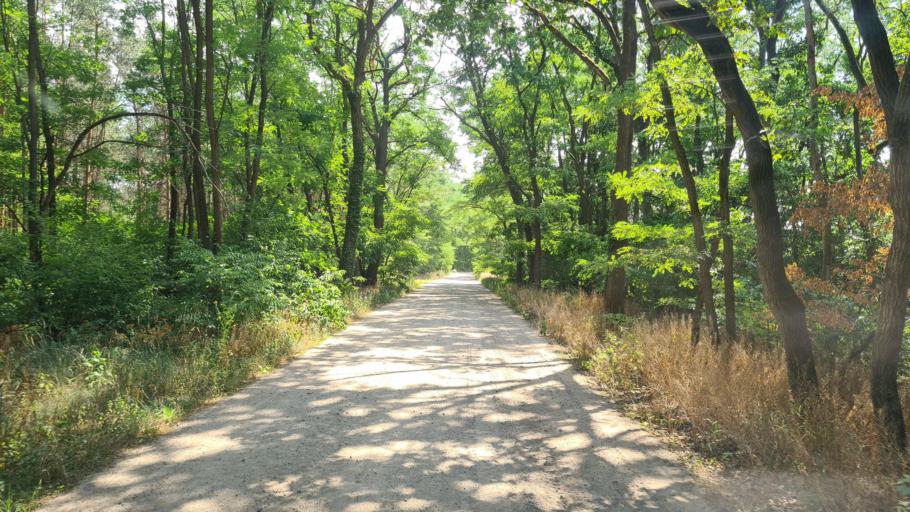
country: DE
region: Brandenburg
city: Golzow
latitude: 52.3224
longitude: 12.5520
